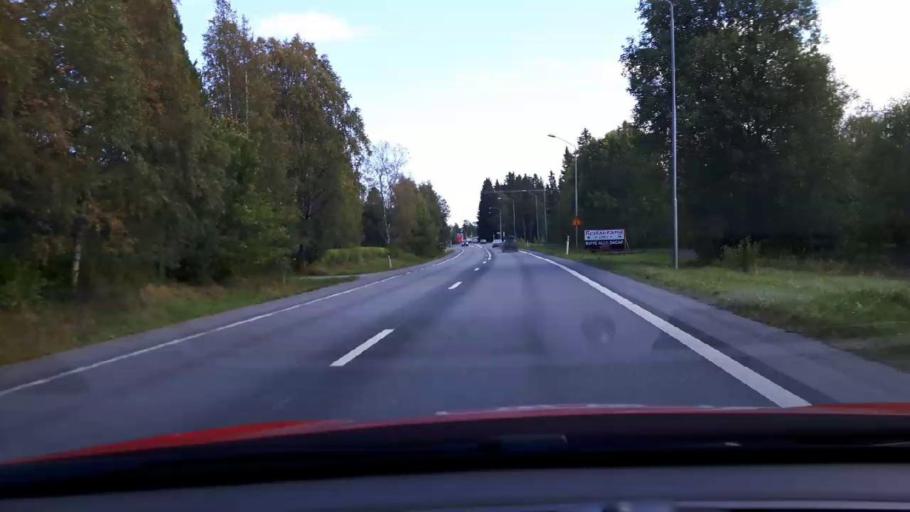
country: SE
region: Jaemtland
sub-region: OEstersunds Kommun
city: Brunflo
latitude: 63.0872
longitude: 14.8118
